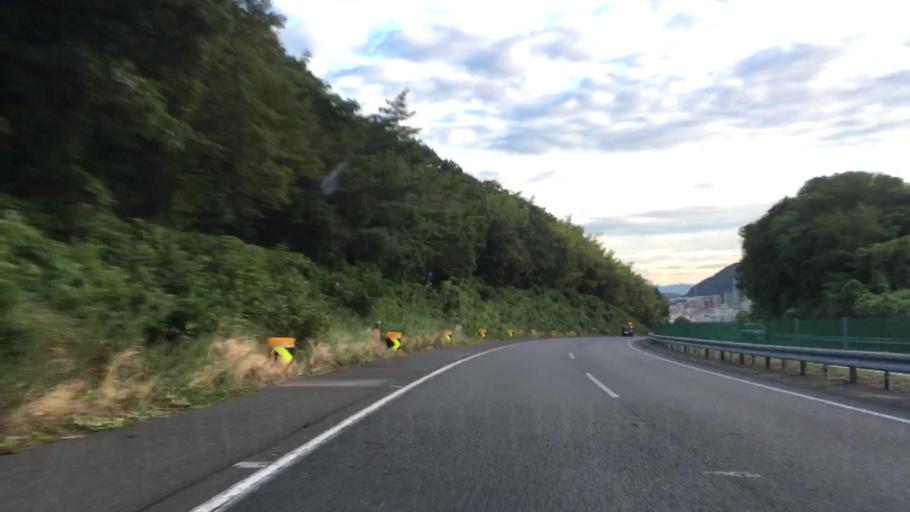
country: JP
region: Yamaguchi
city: Shimonoseki
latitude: 34.0227
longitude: 130.9603
